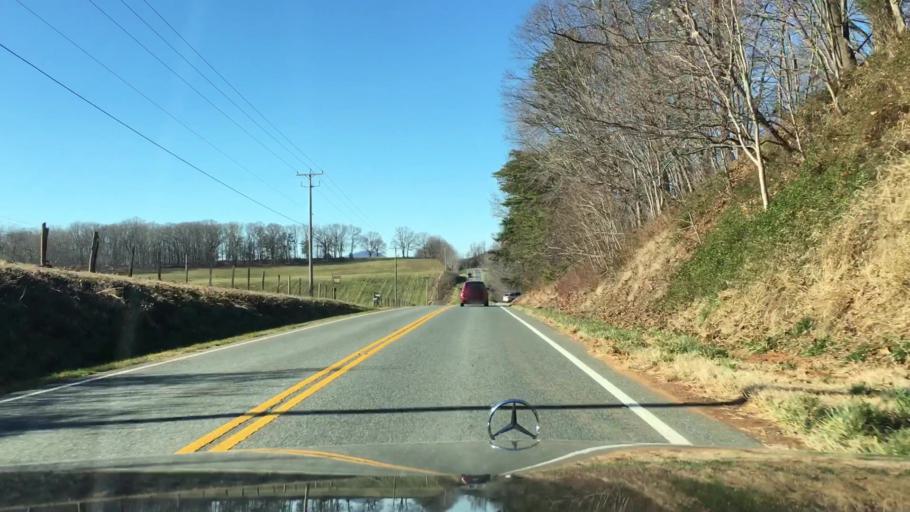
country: US
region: Virginia
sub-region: Franklin County
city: North Shore
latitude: 37.2456
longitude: -79.6833
